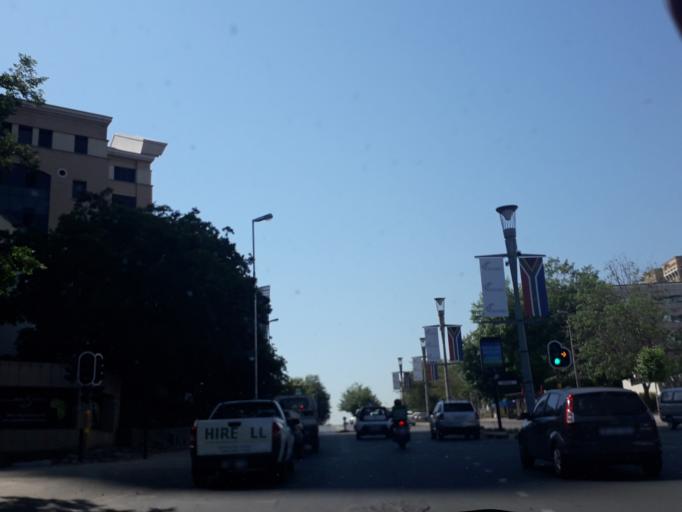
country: ZA
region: Gauteng
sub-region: City of Johannesburg Metropolitan Municipality
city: Johannesburg
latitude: -26.1044
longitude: 28.0540
